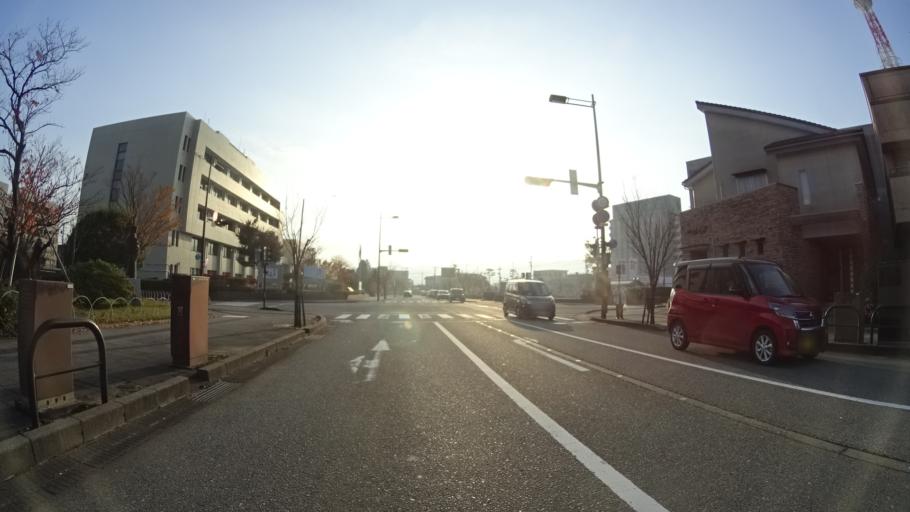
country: JP
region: Ishikawa
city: Nanao
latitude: 37.0431
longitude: 136.9662
